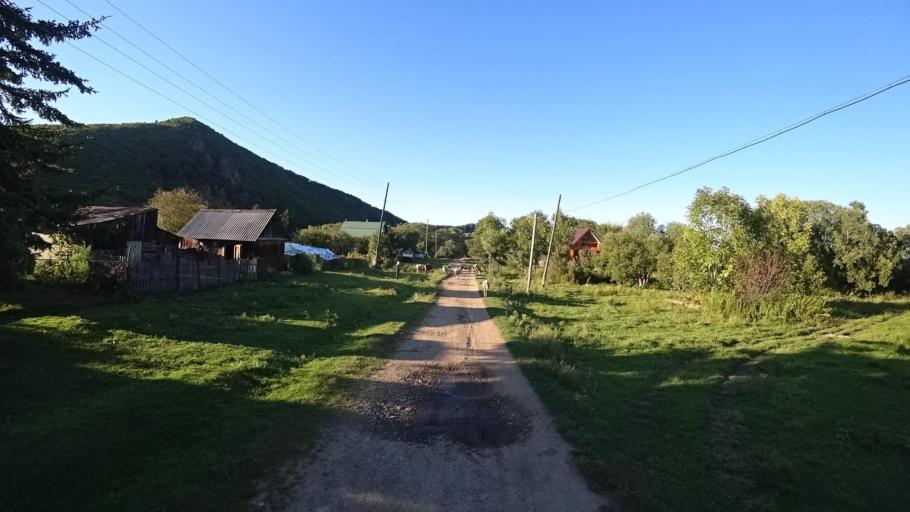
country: RU
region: Primorskiy
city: Kirovskiy
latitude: 44.8338
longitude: 133.5756
